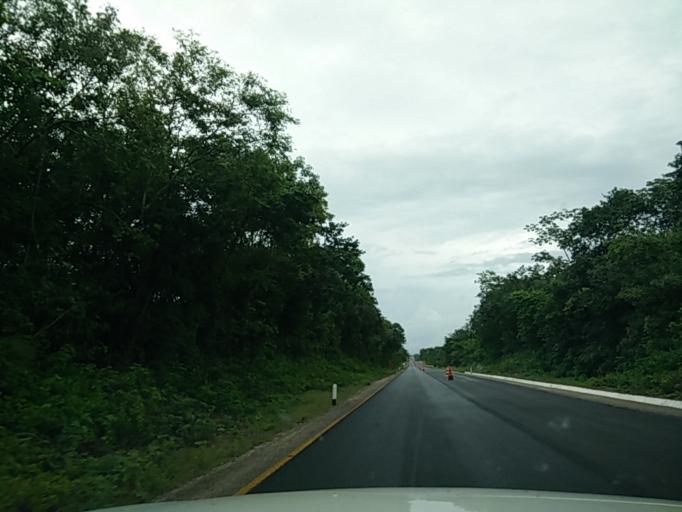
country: MX
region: Quintana Roo
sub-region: Lazaro Cardenas
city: El Tintal
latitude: 20.8987
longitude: -87.4775
